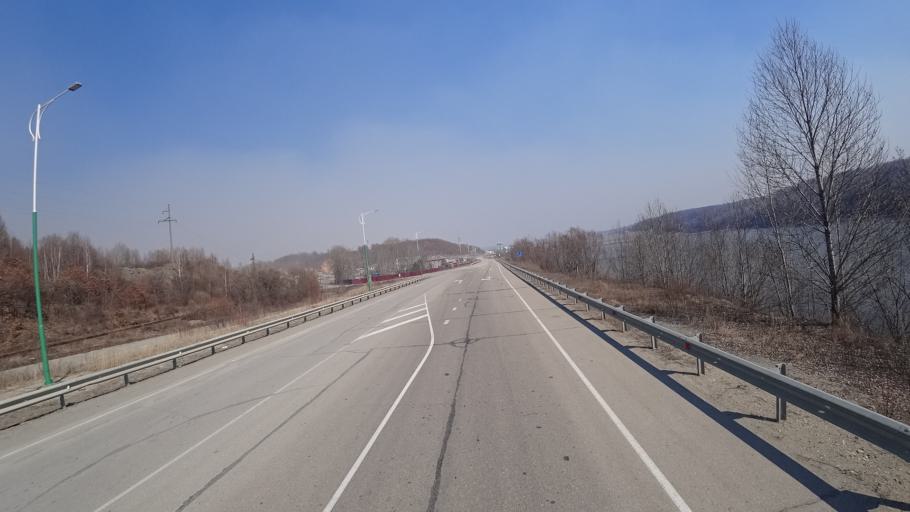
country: RU
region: Amur
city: Novobureyskiy
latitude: 49.7882
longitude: 129.9574
